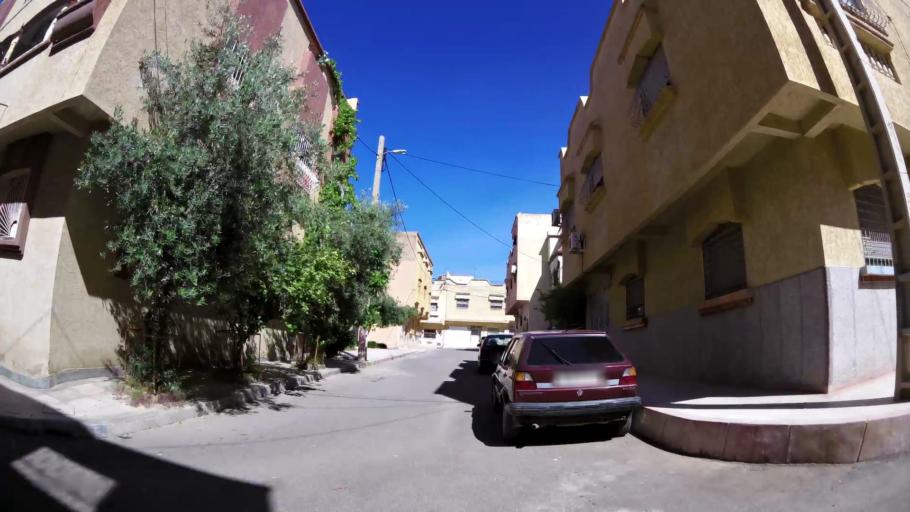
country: MA
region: Oriental
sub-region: Oujda-Angad
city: Oujda
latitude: 34.6565
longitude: -1.9181
